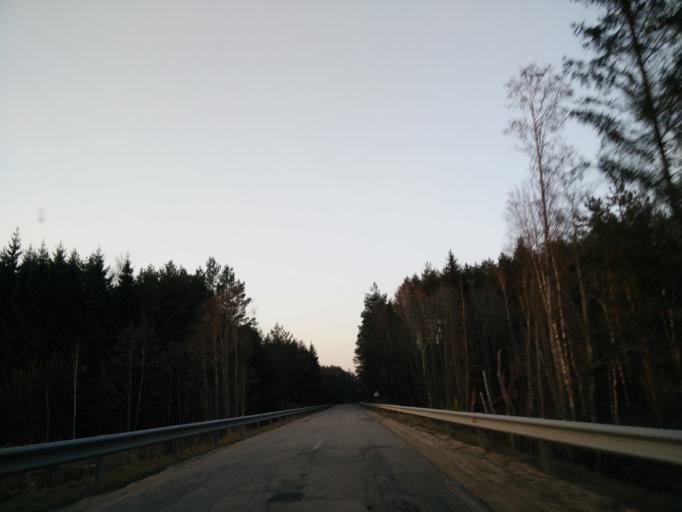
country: LT
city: Trakai
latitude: 54.7012
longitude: 24.9645
